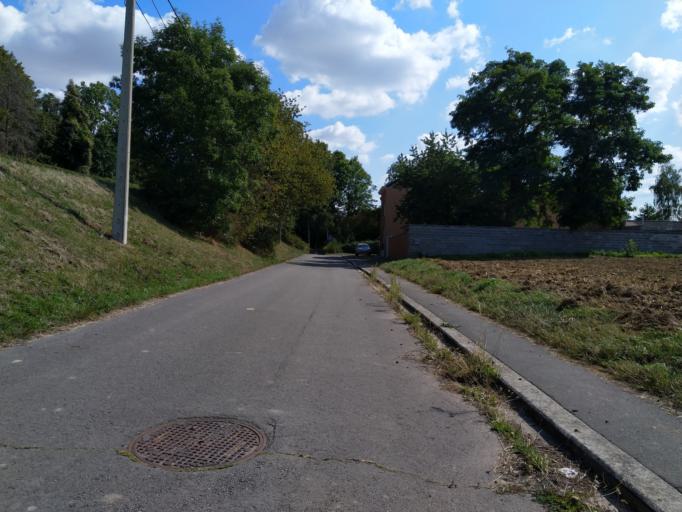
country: BE
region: Wallonia
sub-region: Province du Hainaut
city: Chasse Royale
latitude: 50.4294
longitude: 3.9334
